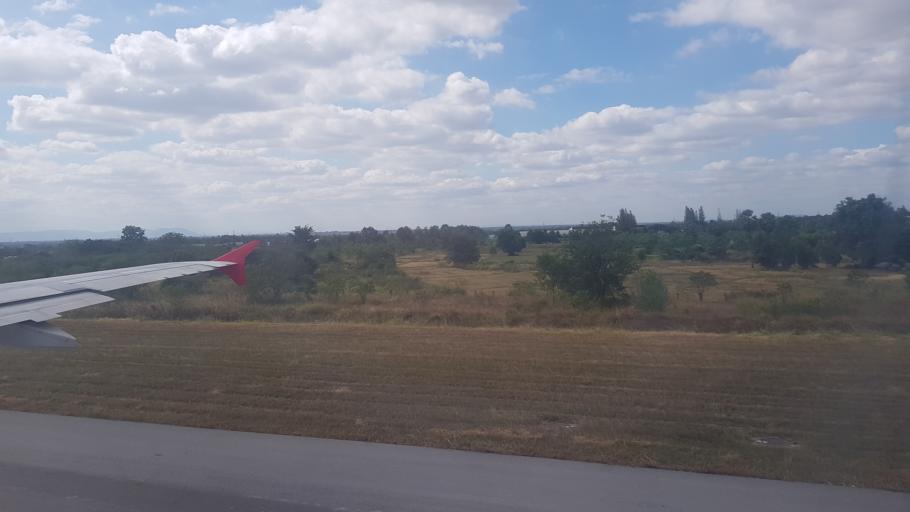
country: TH
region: Khon Kaen
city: Khon Kaen
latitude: 16.4555
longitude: 102.7759
